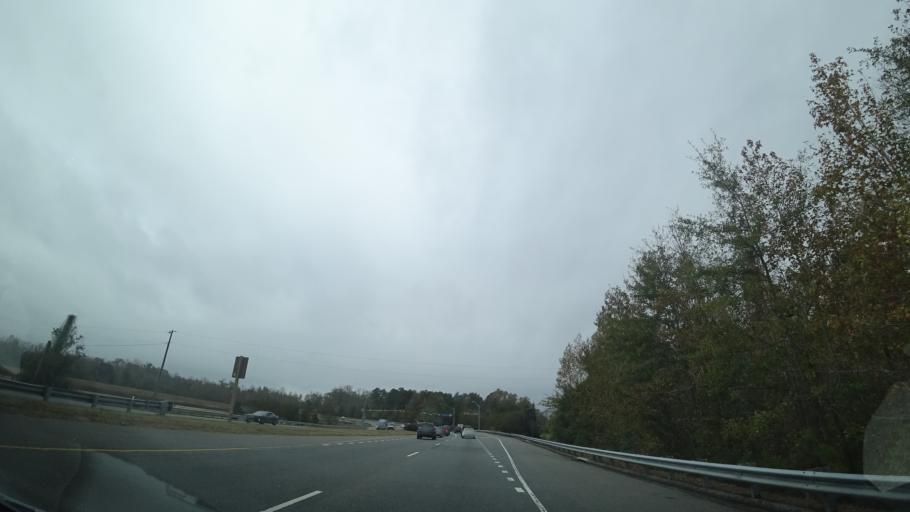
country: US
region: North Carolina
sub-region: Currituck County
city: Moyock
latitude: 36.5652
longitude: -76.1994
